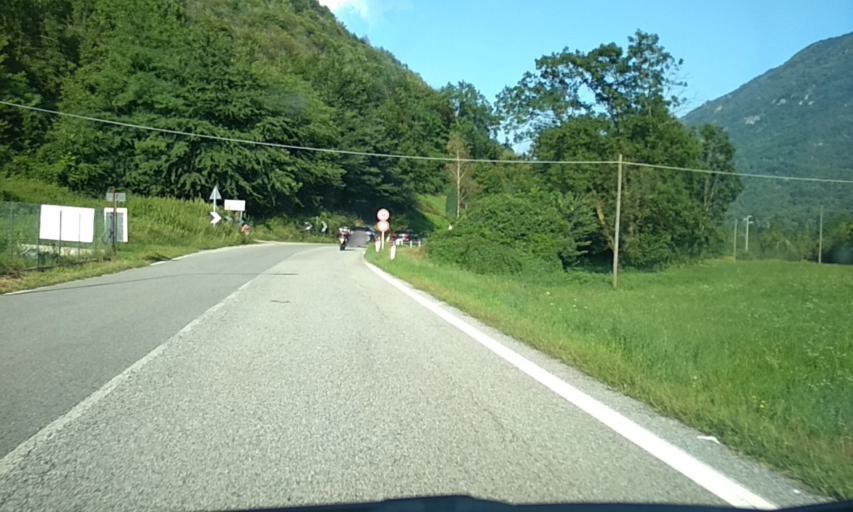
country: IT
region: Piedmont
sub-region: Provincia di Torino
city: Sparone
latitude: 45.4078
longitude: 7.5222
